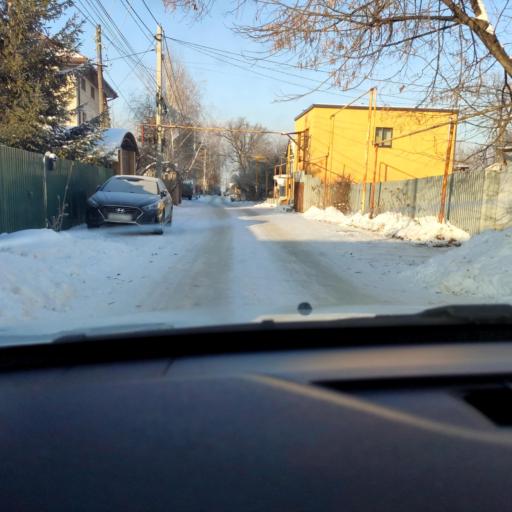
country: RU
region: Samara
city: Samara
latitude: 53.2722
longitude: 50.2029
